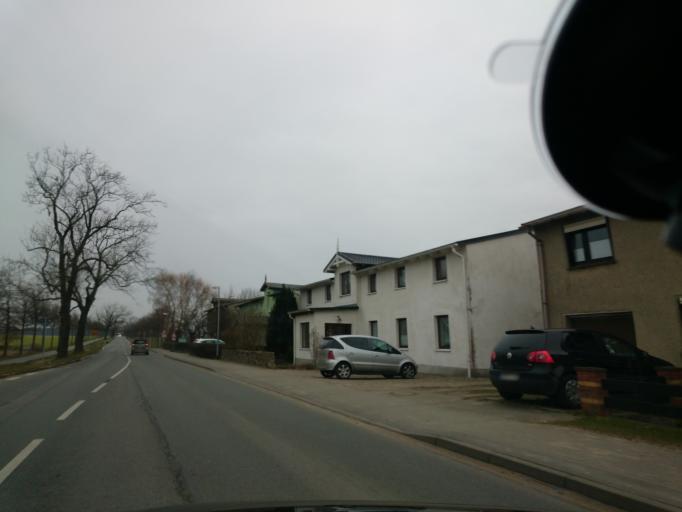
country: DE
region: Mecklenburg-Vorpommern
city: Borgerende-Rethwisch
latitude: 54.1411
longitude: 11.9364
